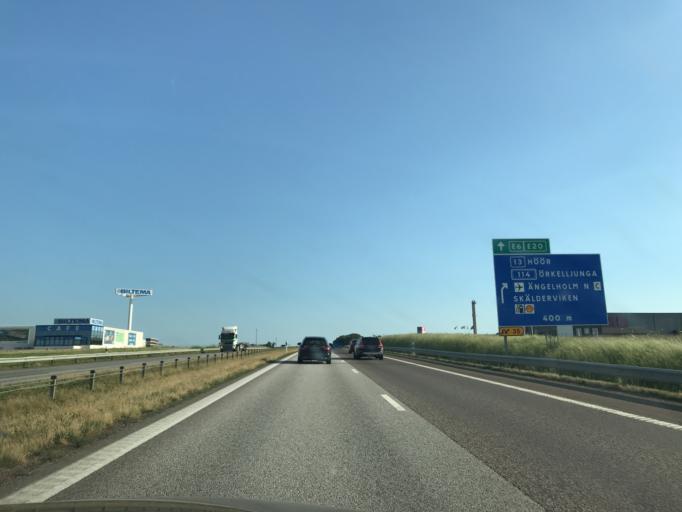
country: SE
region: Skane
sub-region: Angelholms Kommun
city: AEngelholm
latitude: 56.2412
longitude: 12.8990
